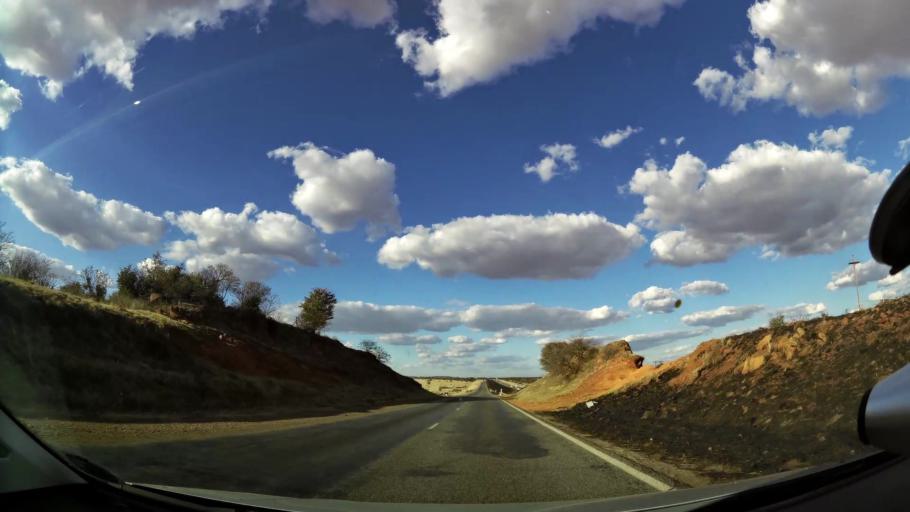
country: ZA
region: North-West
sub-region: Dr Kenneth Kaunda District Municipality
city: Stilfontein
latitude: -26.7887
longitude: 26.9253
